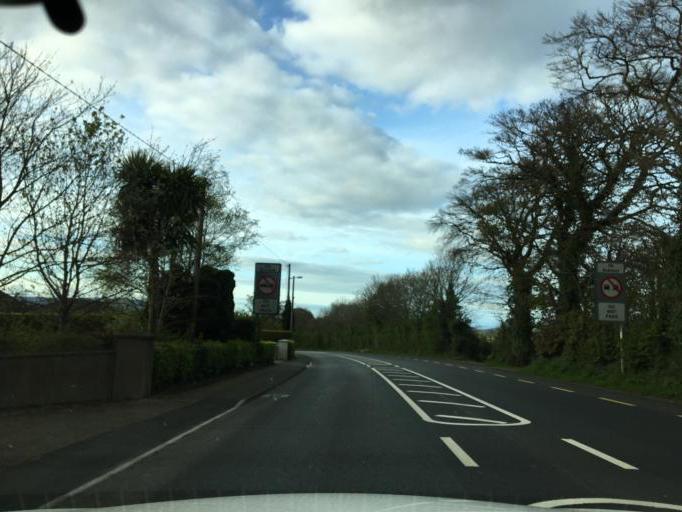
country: IE
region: Leinster
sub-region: Loch Garman
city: New Ross
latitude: 52.4107
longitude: -6.9348
